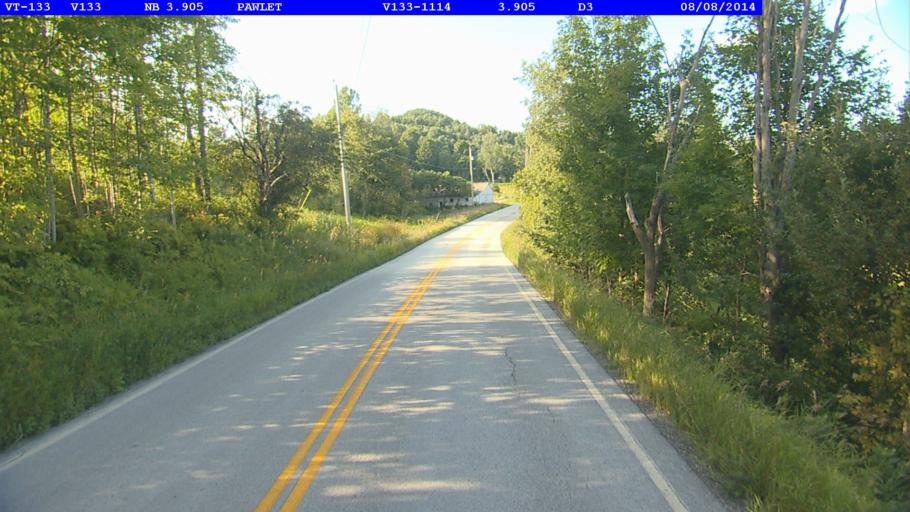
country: US
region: New York
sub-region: Washington County
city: Granville
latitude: 43.3860
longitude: -73.1369
